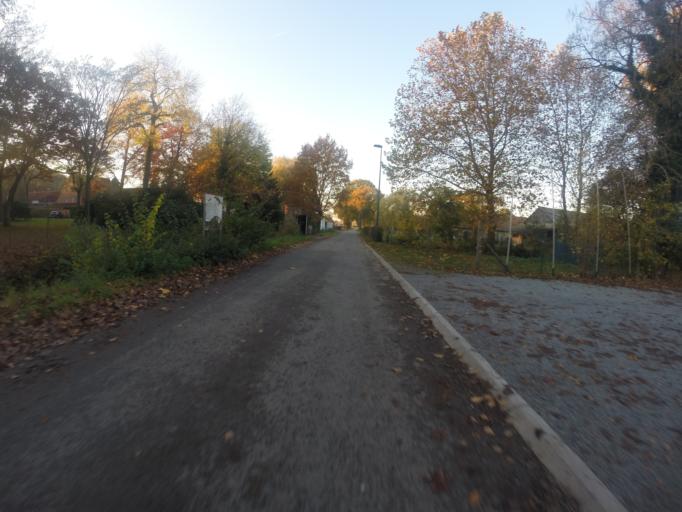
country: BE
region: Flanders
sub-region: Provincie Oost-Vlaanderen
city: Aalter
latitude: 51.0999
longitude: 3.4287
